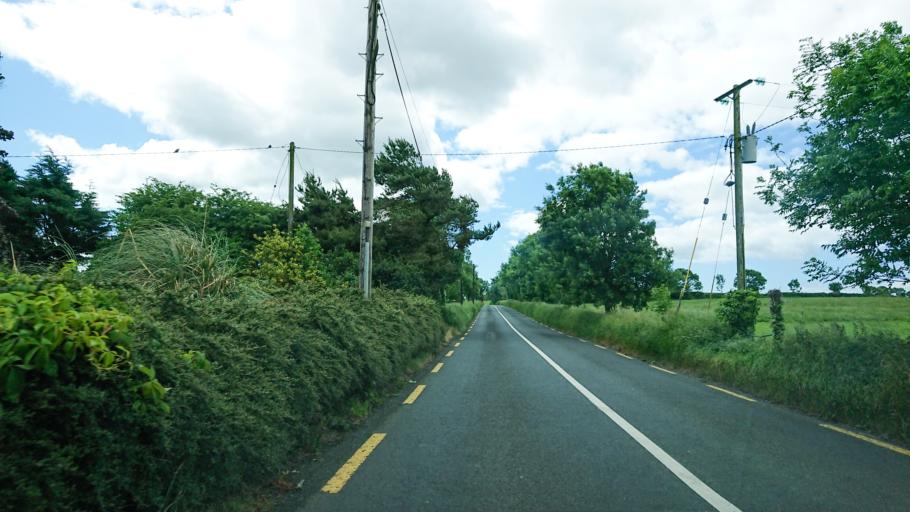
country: IE
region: Munster
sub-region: Waterford
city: Tra Mhor
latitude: 52.2194
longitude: -7.1980
